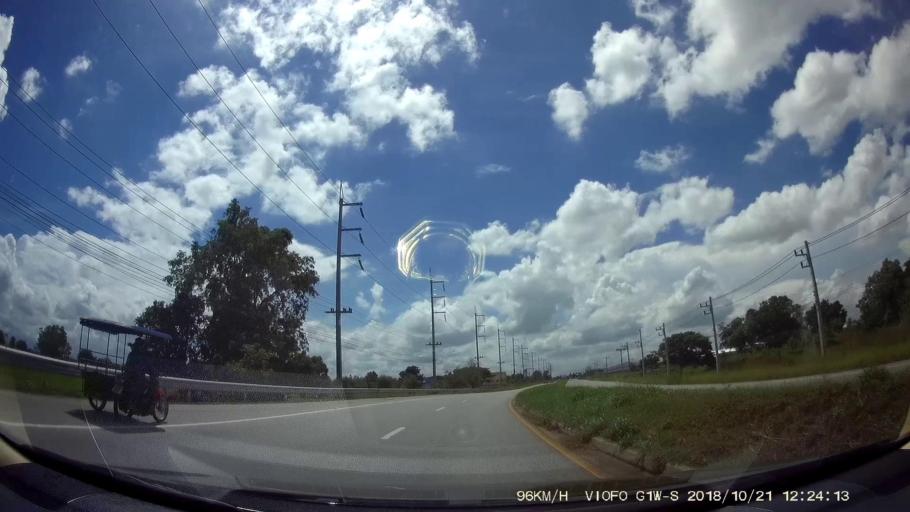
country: TH
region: Nakhon Ratchasima
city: Dan Khun Thot
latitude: 15.2352
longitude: 101.7862
